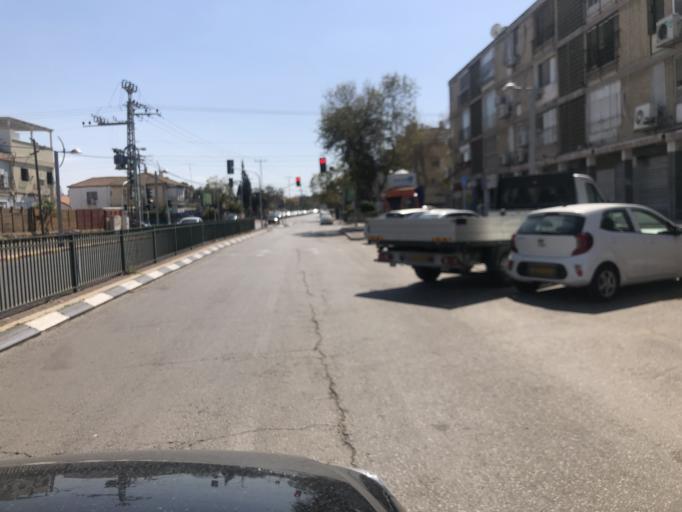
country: IL
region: Tel Aviv
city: Holon
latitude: 32.0109
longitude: 34.7649
